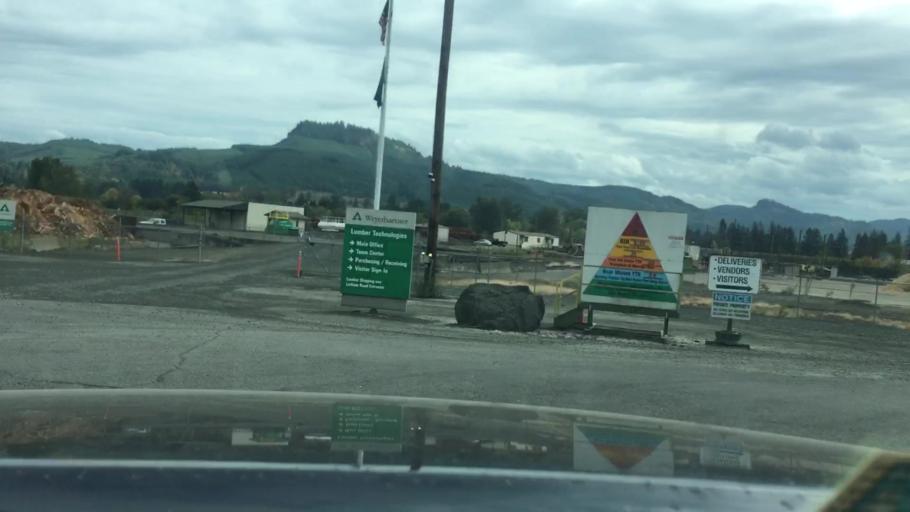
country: US
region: Oregon
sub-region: Lane County
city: Cottage Grove
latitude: 43.7681
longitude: -123.0784
